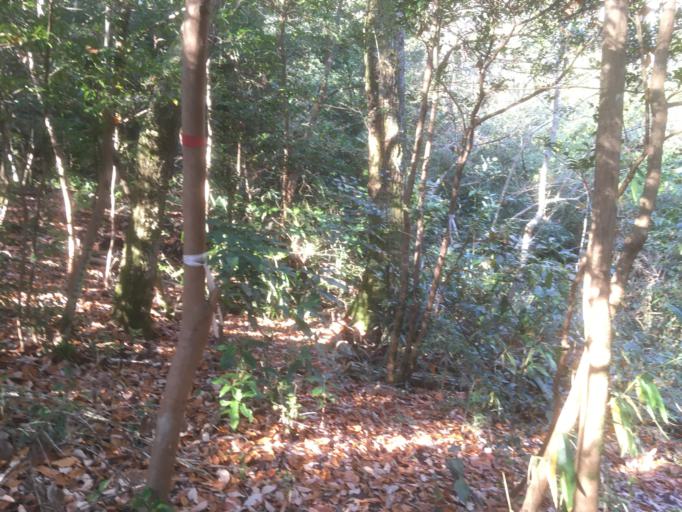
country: JP
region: Nara
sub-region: Ikoma-shi
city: Ikoma
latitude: 34.6921
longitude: 135.6832
